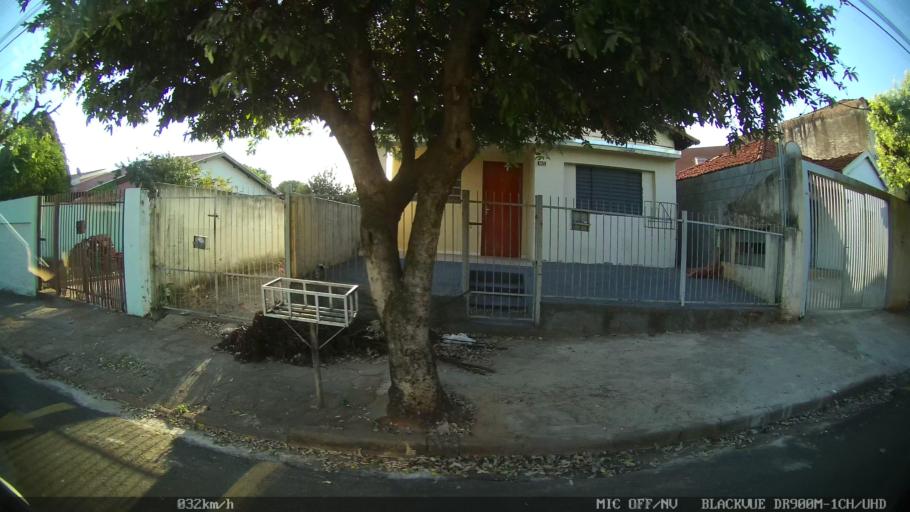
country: BR
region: Sao Paulo
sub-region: Sao Jose Do Rio Preto
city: Sao Jose do Rio Preto
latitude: -20.7954
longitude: -49.3675
